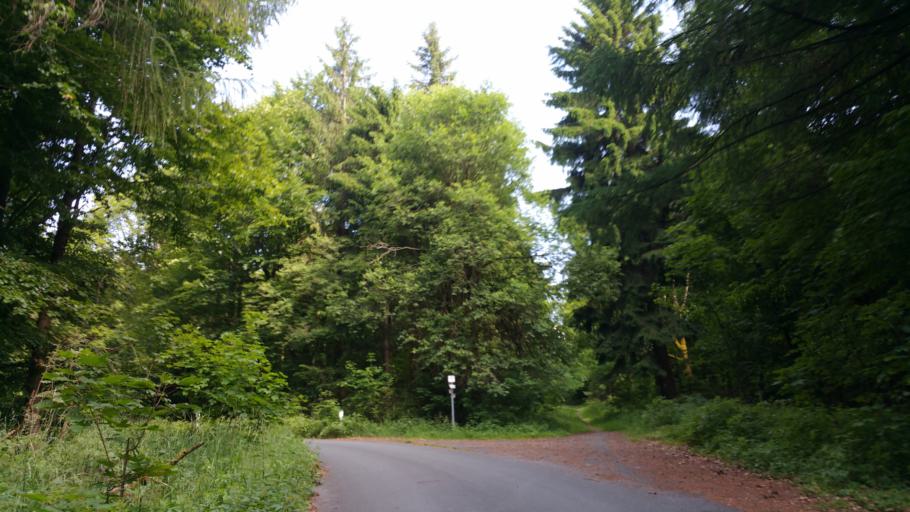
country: DE
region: Bavaria
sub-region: Upper Franconia
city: Marktleuthen
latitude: 50.1845
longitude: 12.0164
